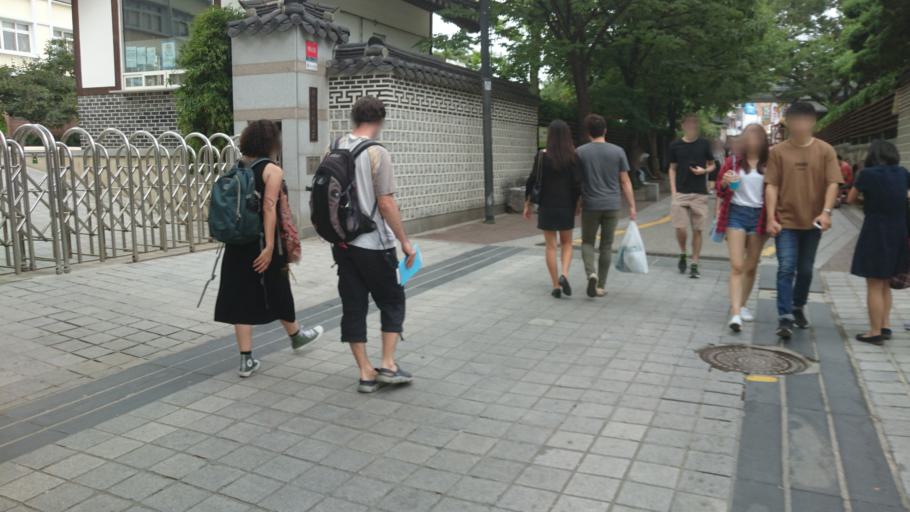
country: KR
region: Seoul
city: Seoul
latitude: 37.5777
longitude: 126.9824
